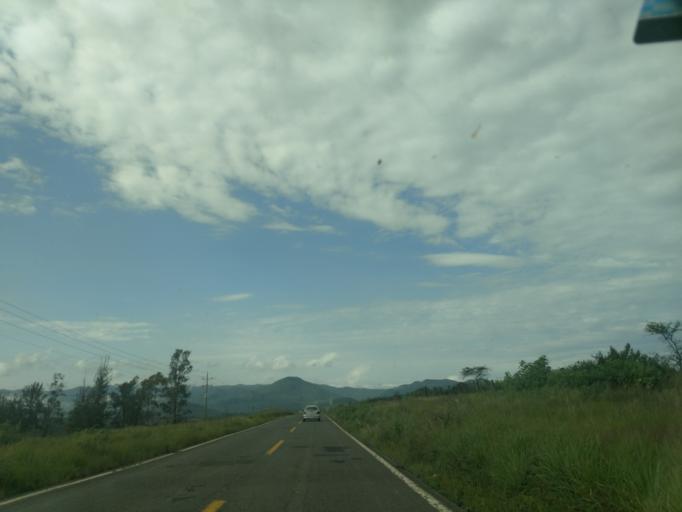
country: MX
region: Jalisco
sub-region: Atengo
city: Soyatlan del Oro
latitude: 20.5423
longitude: -104.3091
